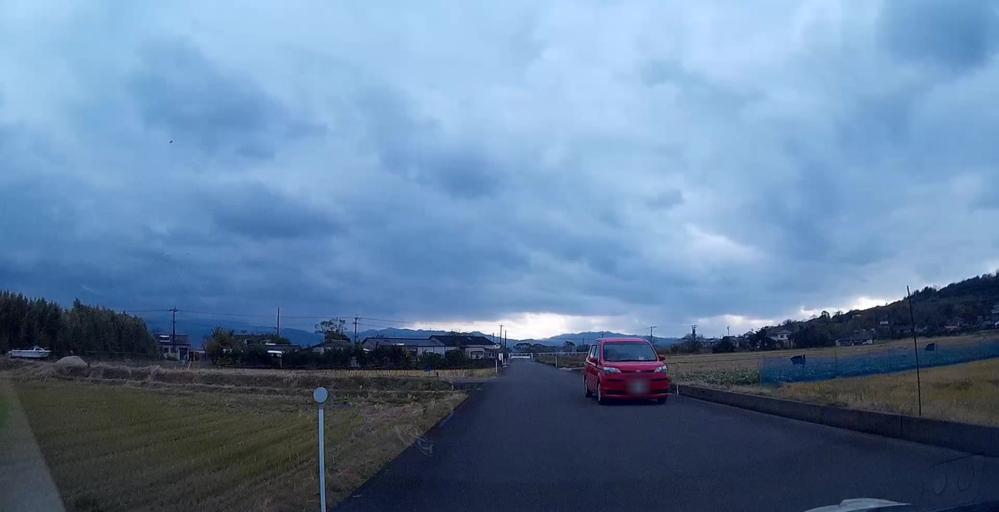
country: JP
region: Kagoshima
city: Izumi
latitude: 32.0973
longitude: 130.2755
